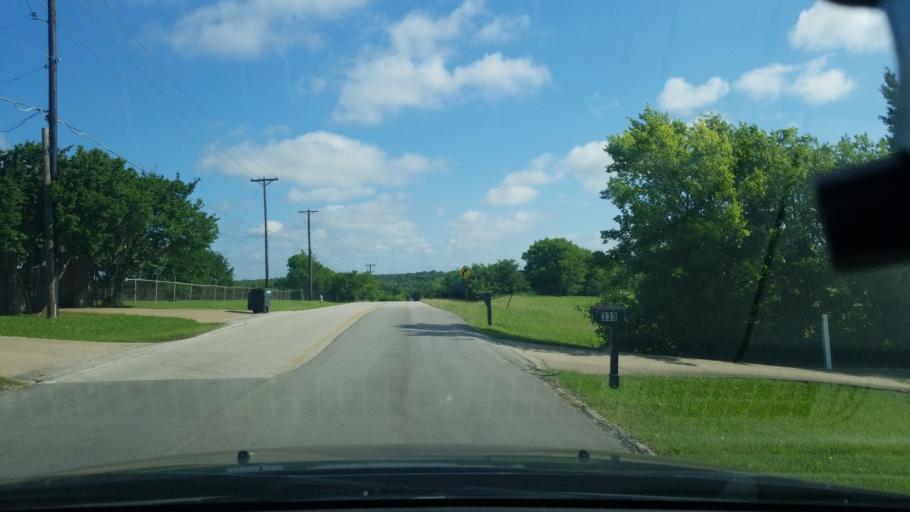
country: US
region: Texas
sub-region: Dallas County
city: Sunnyvale
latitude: 32.8103
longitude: -96.5608
